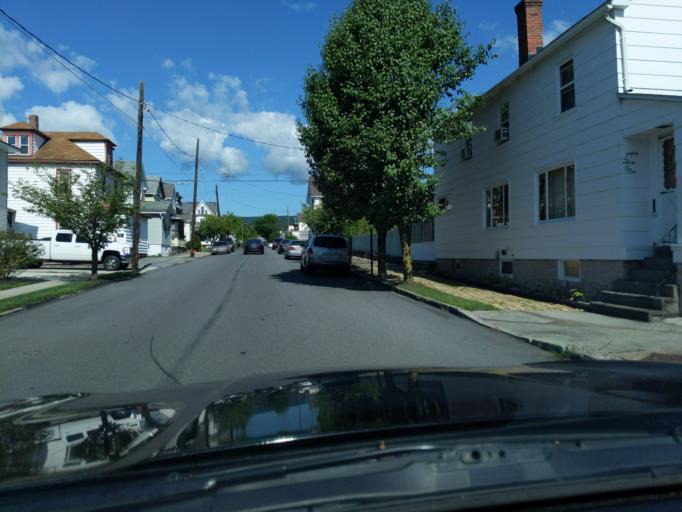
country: US
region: Pennsylvania
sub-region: Blair County
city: Altoona
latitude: 40.5352
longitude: -78.3867
